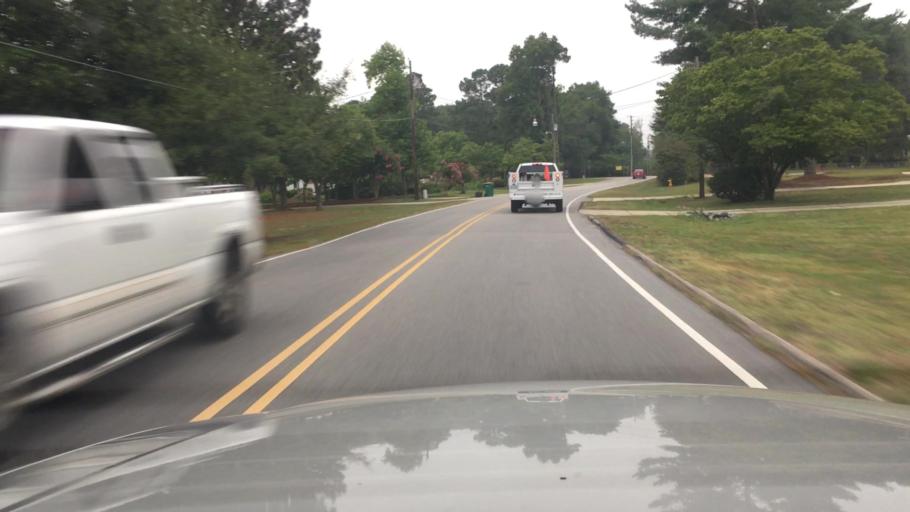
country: US
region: North Carolina
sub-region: Cumberland County
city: Hope Mills
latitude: 34.9746
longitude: -78.9399
